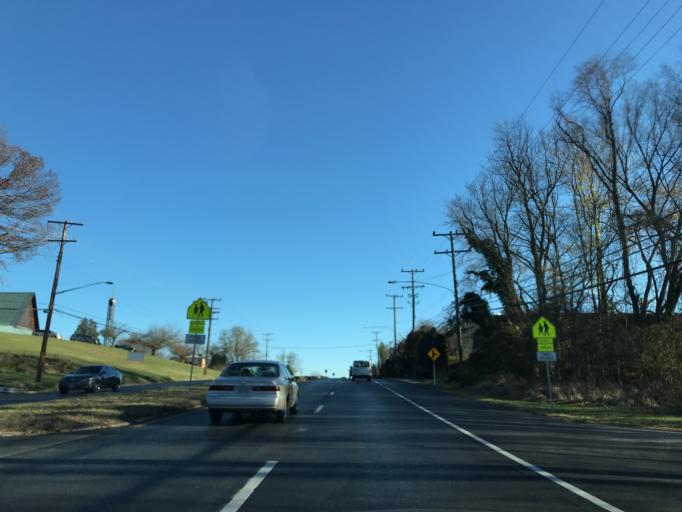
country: US
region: Maryland
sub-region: Montgomery County
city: North Bethesda
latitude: 39.0657
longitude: -77.0992
